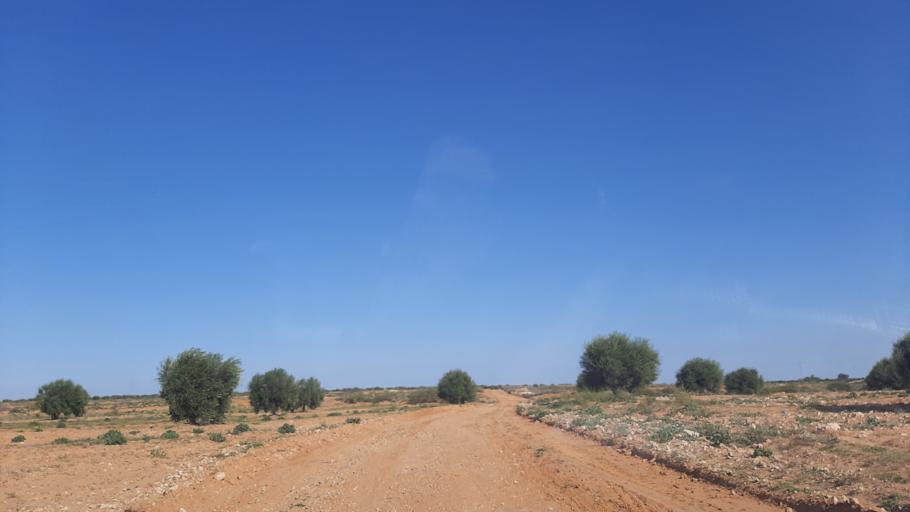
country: TN
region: Madanin
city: Medenine
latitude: 33.2805
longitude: 10.7772
